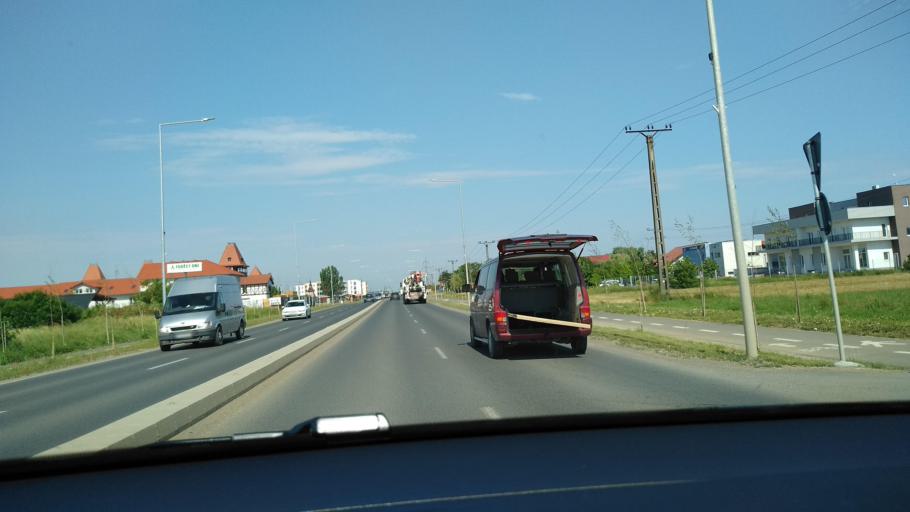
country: RO
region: Timis
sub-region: Comuna Mosnita Noua
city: Mosnita Noua
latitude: 45.7232
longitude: 21.2988
